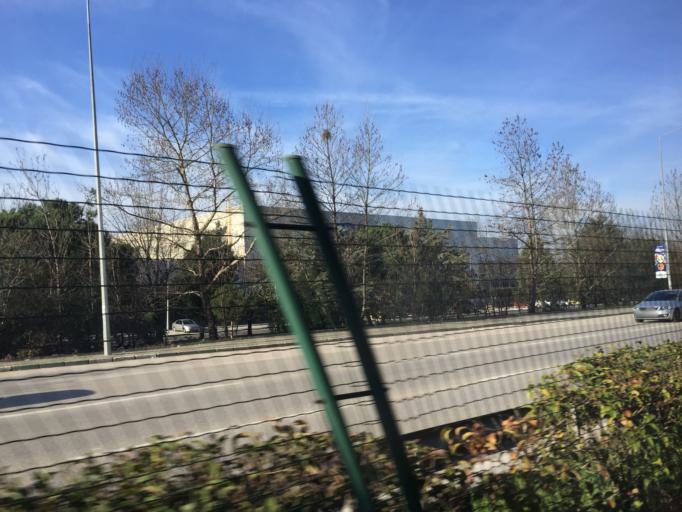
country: TR
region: Bursa
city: Niluefer
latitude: 40.2416
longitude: 28.9694
